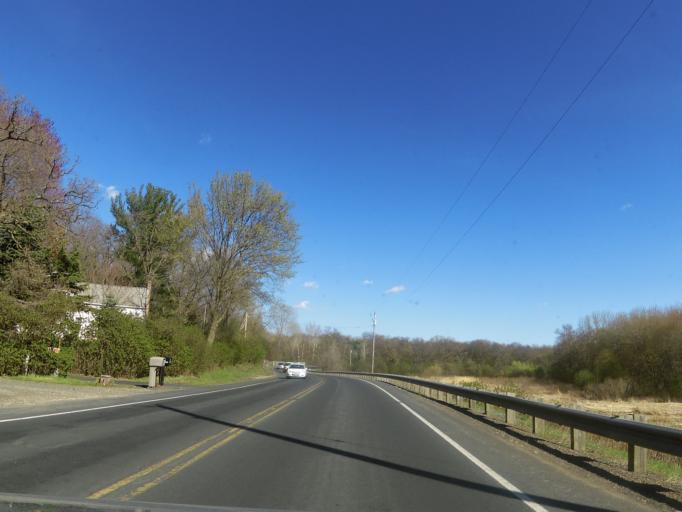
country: US
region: Wisconsin
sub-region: Saint Croix County
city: Somerset
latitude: 45.0277
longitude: -92.6625
